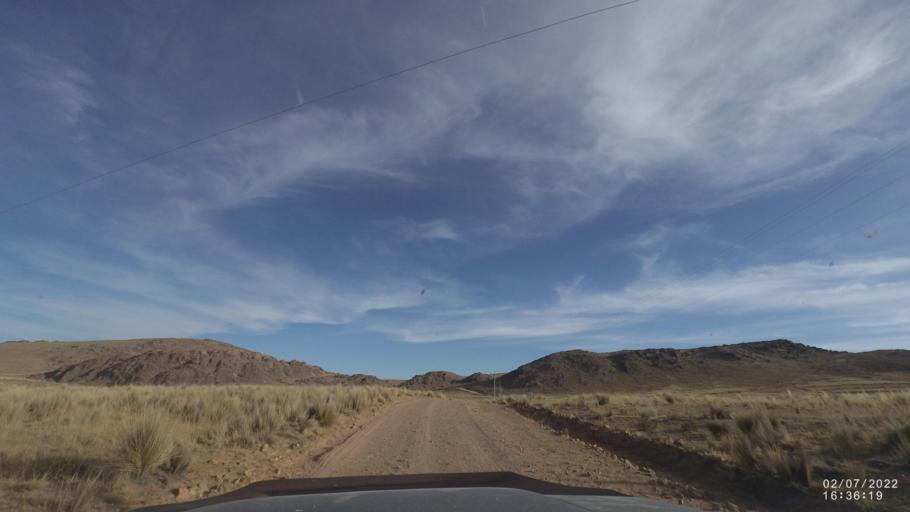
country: BO
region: Cochabamba
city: Irpa Irpa
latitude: -17.9616
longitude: -66.4946
